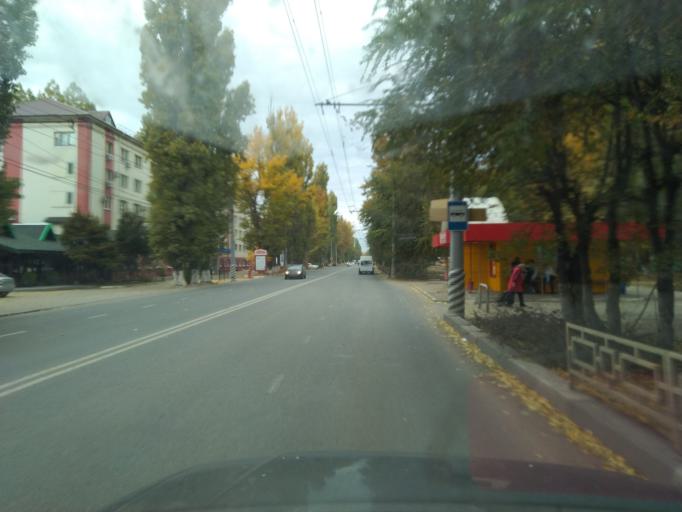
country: RU
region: Saratov
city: Engel's
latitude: 51.4739
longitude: 46.1325
